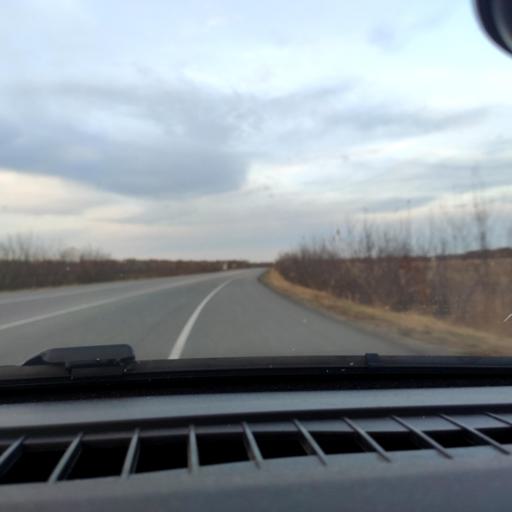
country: RU
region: Voronezj
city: Devitsa
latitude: 51.6039
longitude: 38.9718
